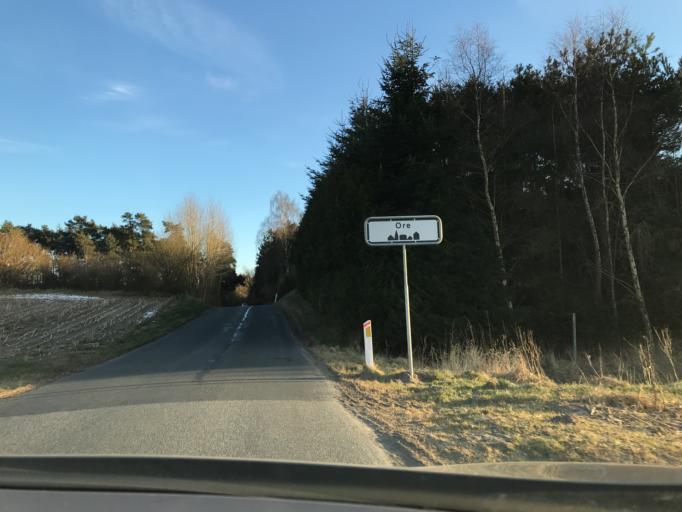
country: DK
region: South Denmark
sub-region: Middelfart Kommune
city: Brenderup
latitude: 55.5089
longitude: 10.0311
